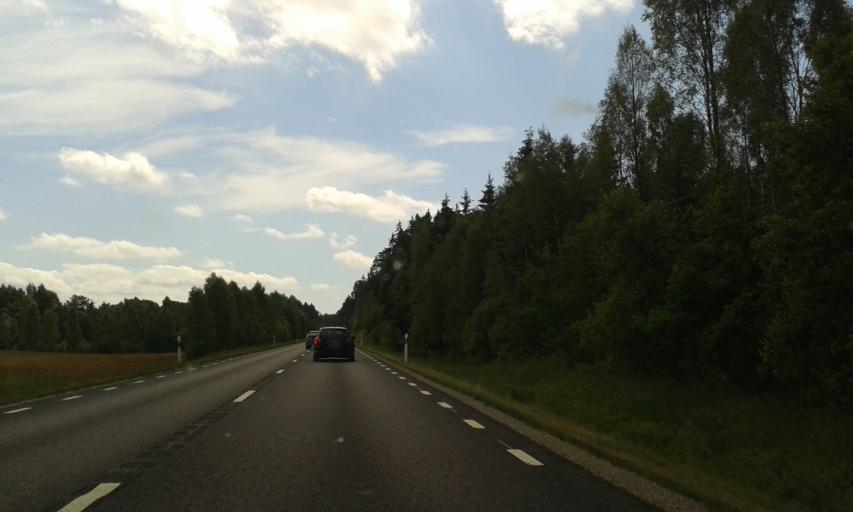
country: SE
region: Joenkoeping
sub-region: Varnamo Kommun
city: Rydaholm
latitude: 57.0186
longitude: 14.2584
